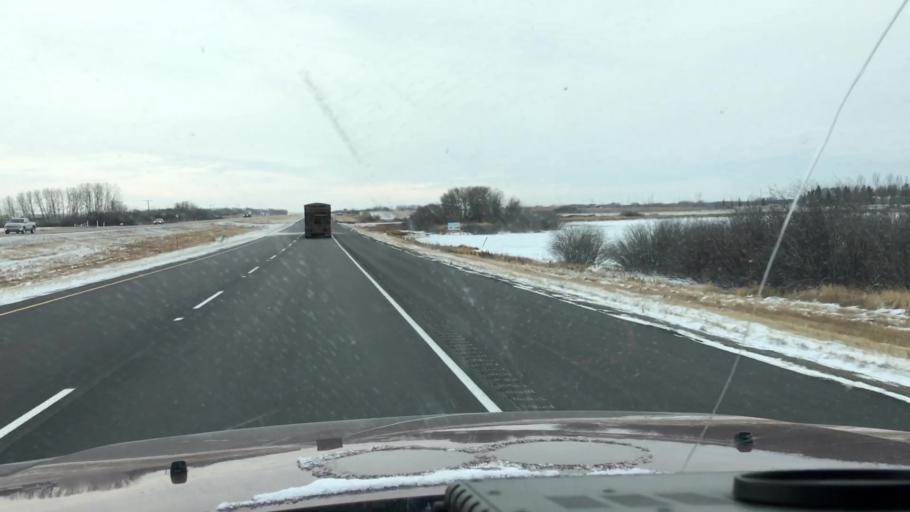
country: CA
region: Saskatchewan
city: Saskatoon
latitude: 51.9234
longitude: -106.5323
